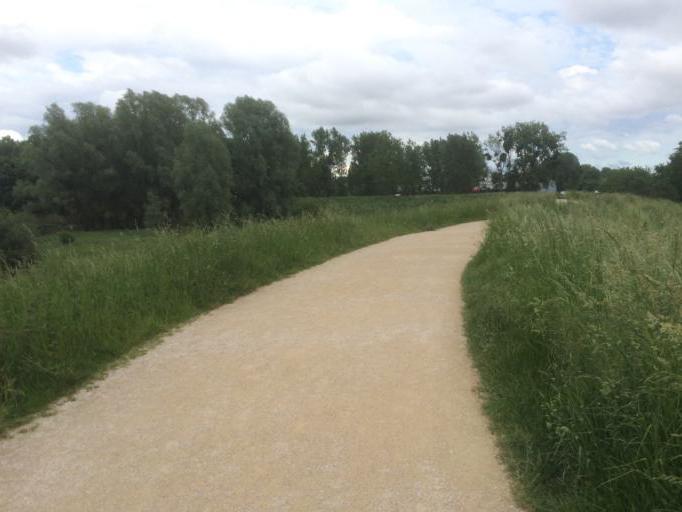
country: FR
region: Ile-de-France
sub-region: Departement de l'Essonne
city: Champlan
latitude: 48.6960
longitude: 2.2819
